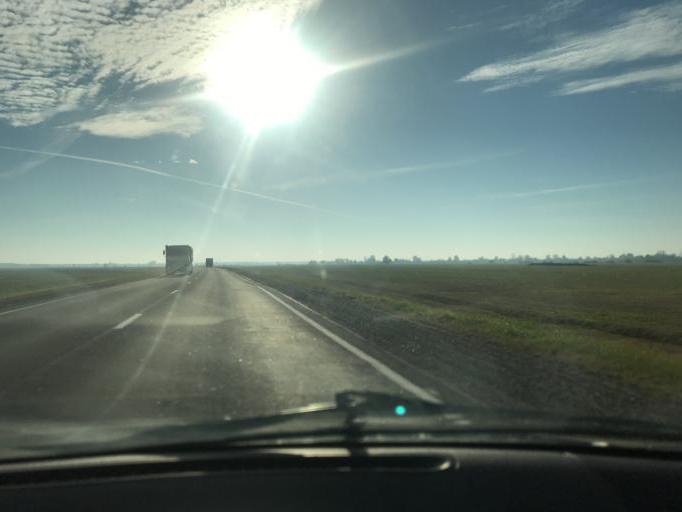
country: BY
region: Brest
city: Drahichyn
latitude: 52.1975
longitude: 25.2398
